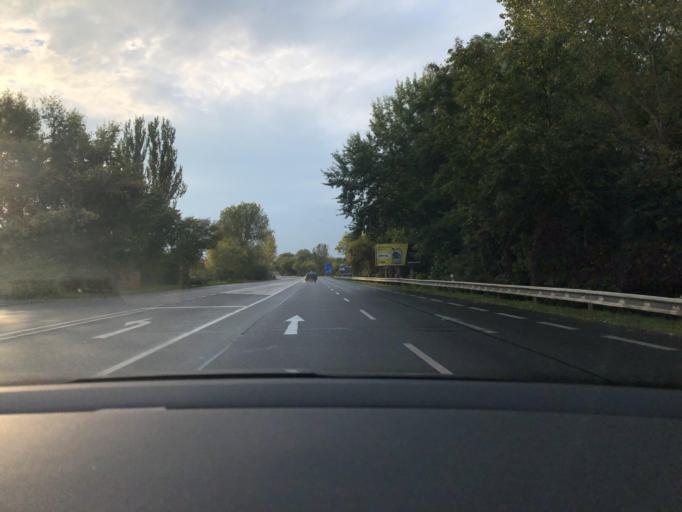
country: CZ
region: Central Bohemia
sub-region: Okres Kolin
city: Kolin
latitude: 50.0326
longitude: 15.1784
